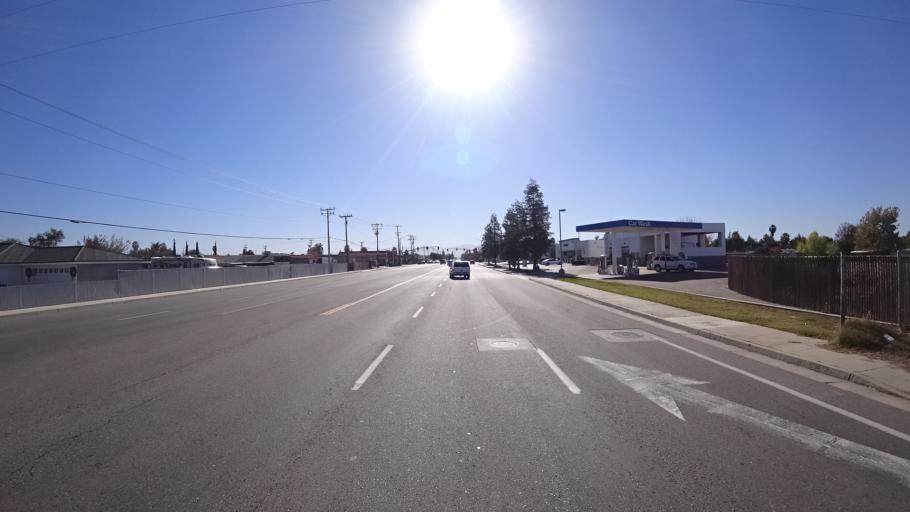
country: US
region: California
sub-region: Kern County
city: Greenfield
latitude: 35.3047
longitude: -119.0568
